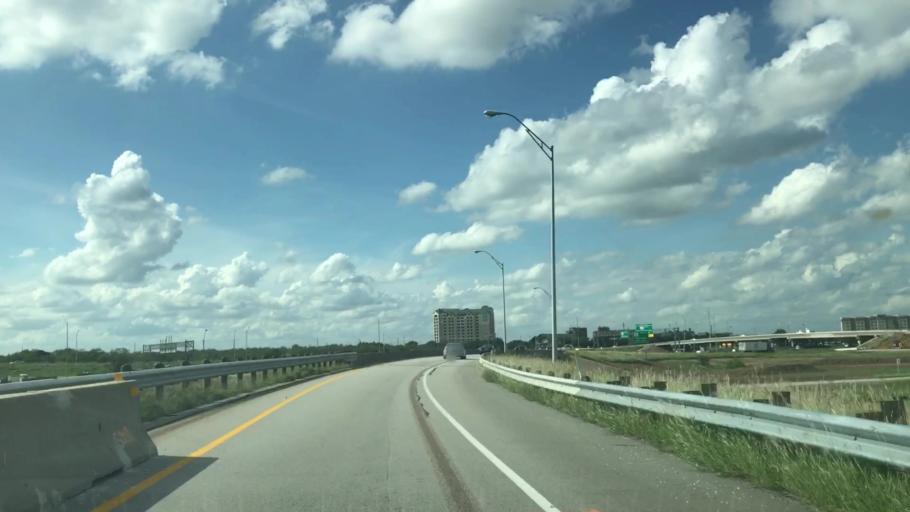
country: US
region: Texas
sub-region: Dallas County
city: Coppell
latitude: 32.9518
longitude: -97.0377
